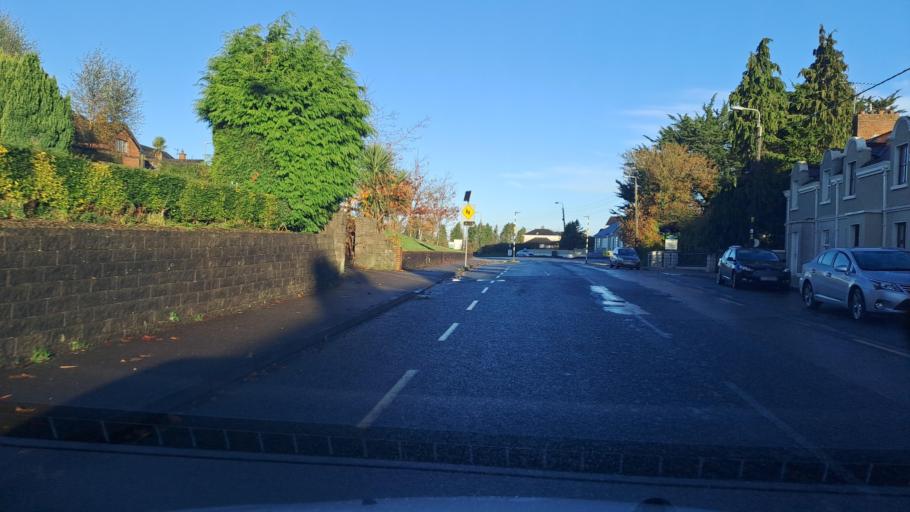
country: IE
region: Ulster
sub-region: An Cabhan
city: Cootehill
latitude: 54.0749
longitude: -7.0858
